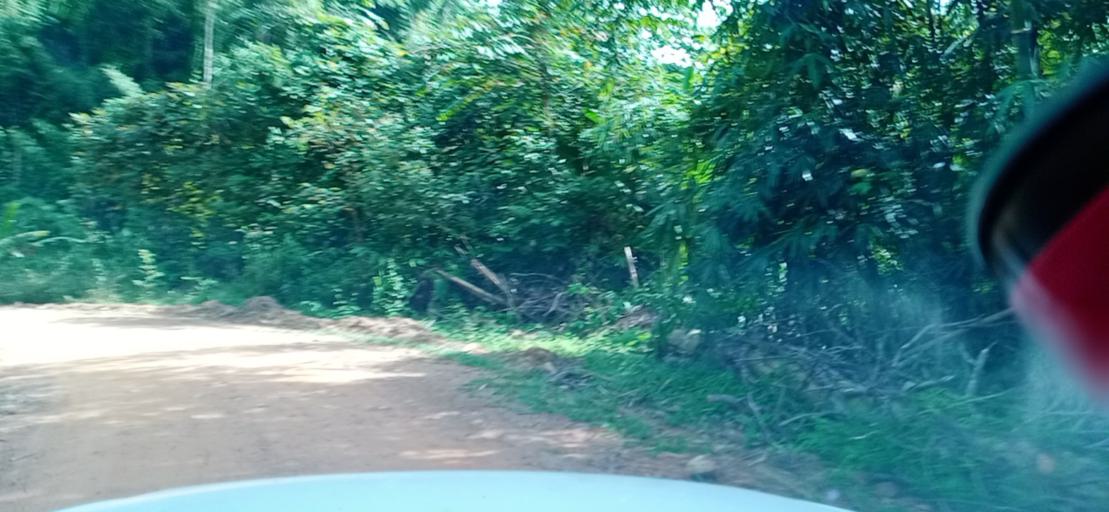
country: TH
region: Changwat Bueng Kan
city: Pak Khat
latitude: 18.6376
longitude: 103.2387
